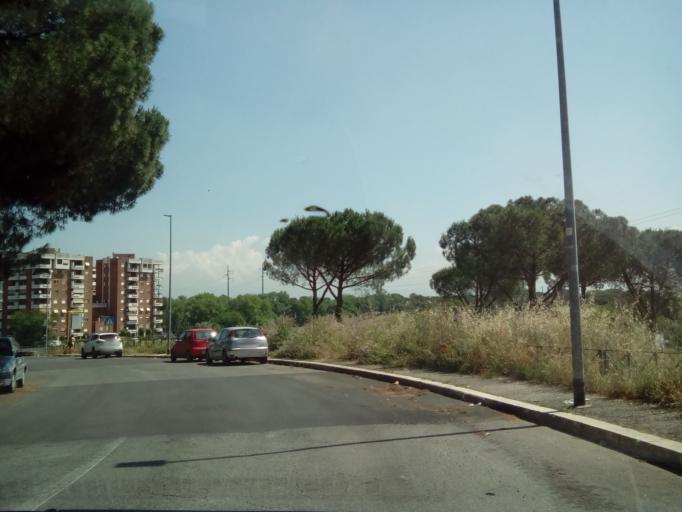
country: IT
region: Latium
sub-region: Citta metropolitana di Roma Capitale
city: Rome
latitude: 41.8809
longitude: 12.5906
